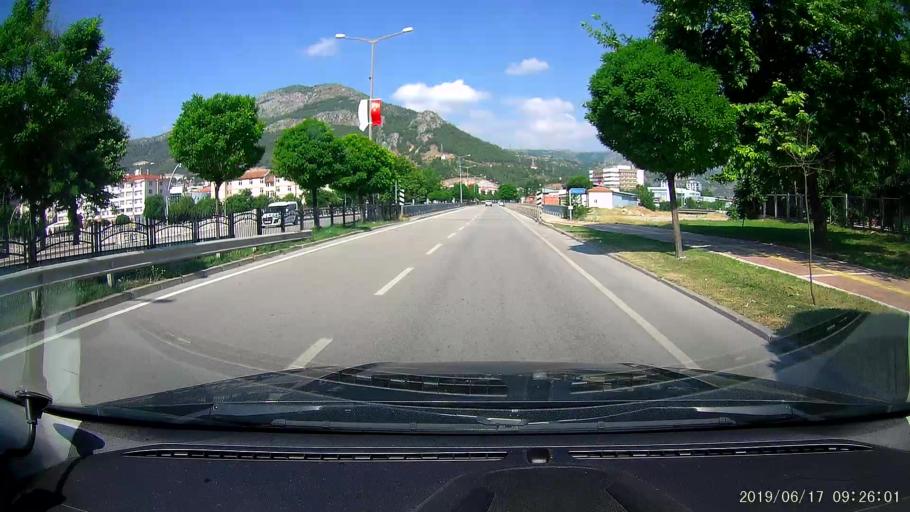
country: TR
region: Amasya
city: Amasya
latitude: 40.6685
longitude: 35.8411
